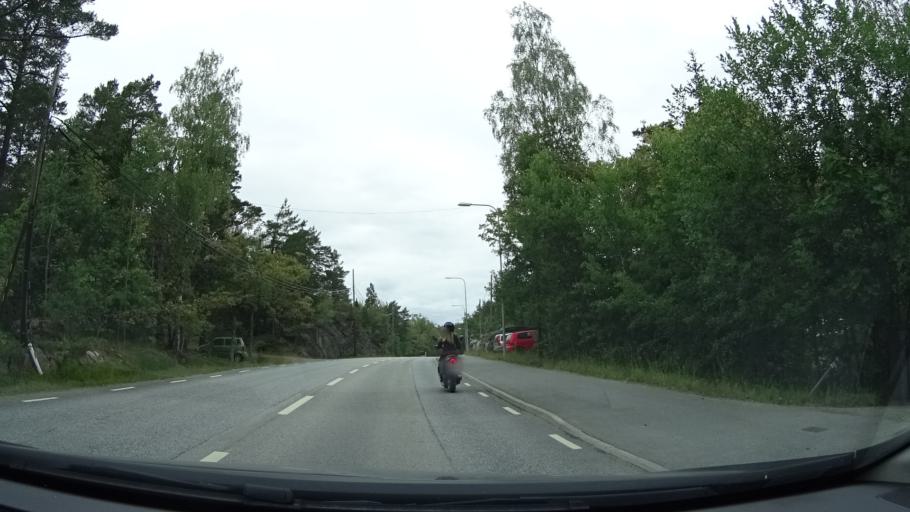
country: SE
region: Stockholm
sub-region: Varmdo Kommun
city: Hemmesta
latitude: 59.3361
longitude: 18.4880
